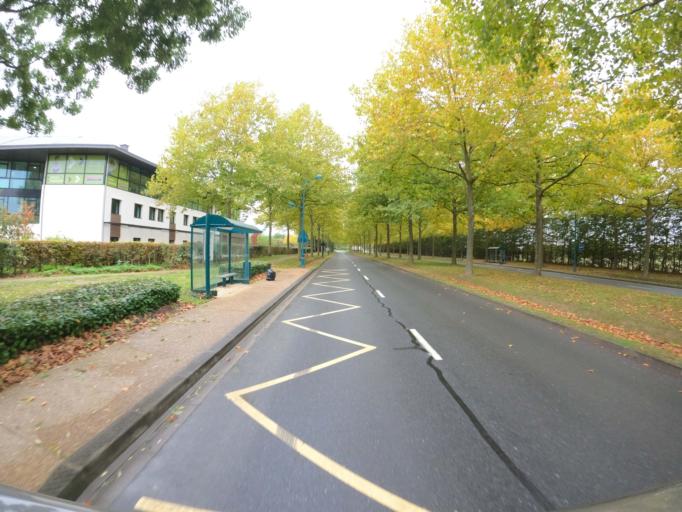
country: FR
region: Ile-de-France
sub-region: Departement de Seine-et-Marne
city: Serris
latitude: 48.8376
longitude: 2.7944
